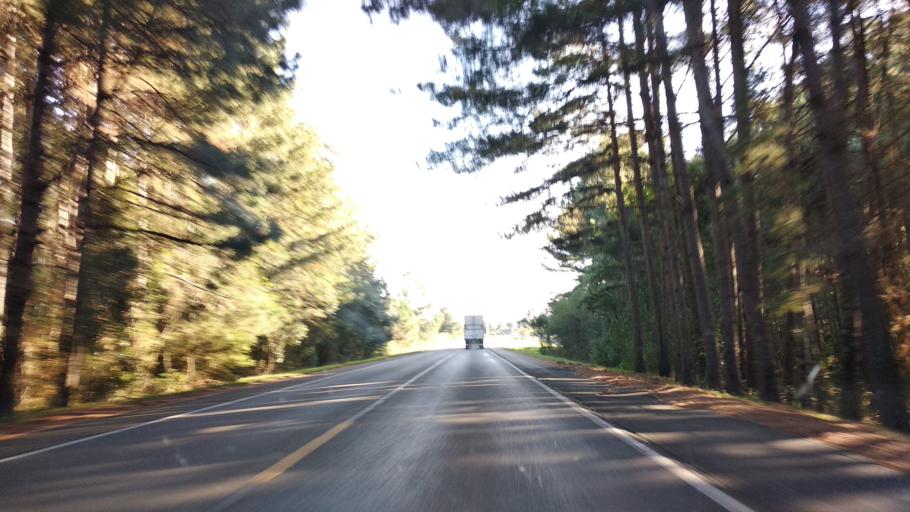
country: BR
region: Santa Catarina
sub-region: Celso Ramos
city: Celso Ramos
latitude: -27.5392
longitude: -51.4103
